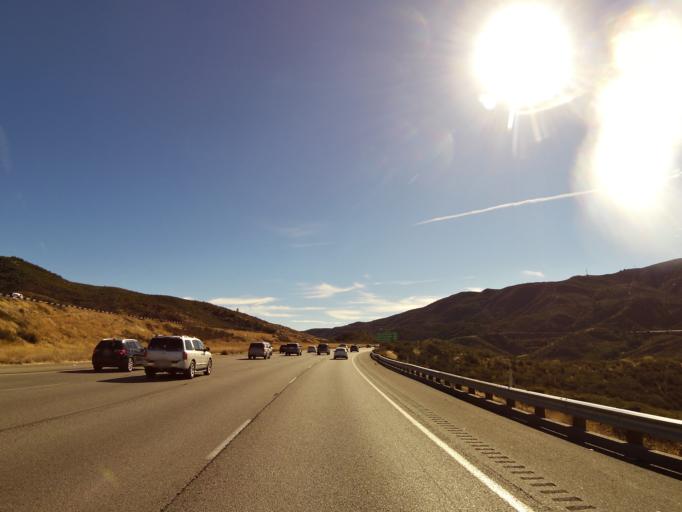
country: US
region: California
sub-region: Los Angeles County
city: Castaic
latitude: 34.6020
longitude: -118.7114
